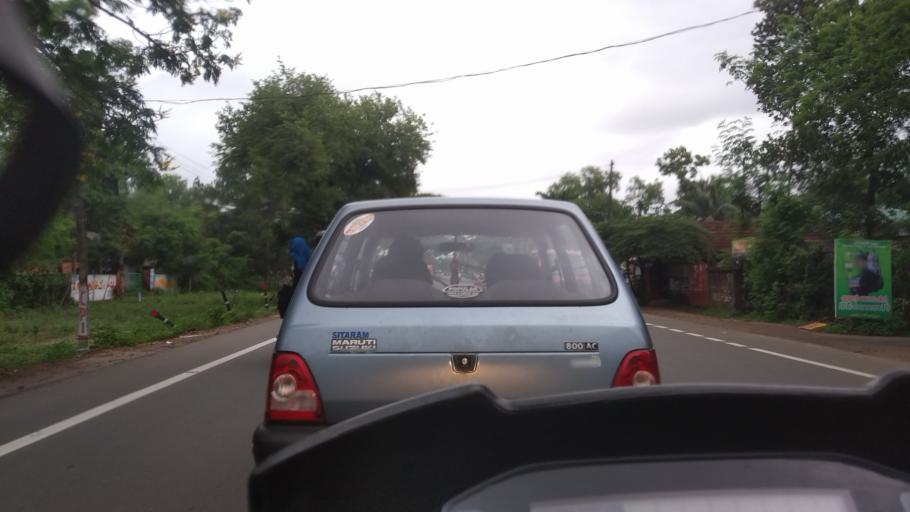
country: IN
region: Kerala
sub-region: Alappuzha
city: Alleppey
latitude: 9.4471
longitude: 76.3425
